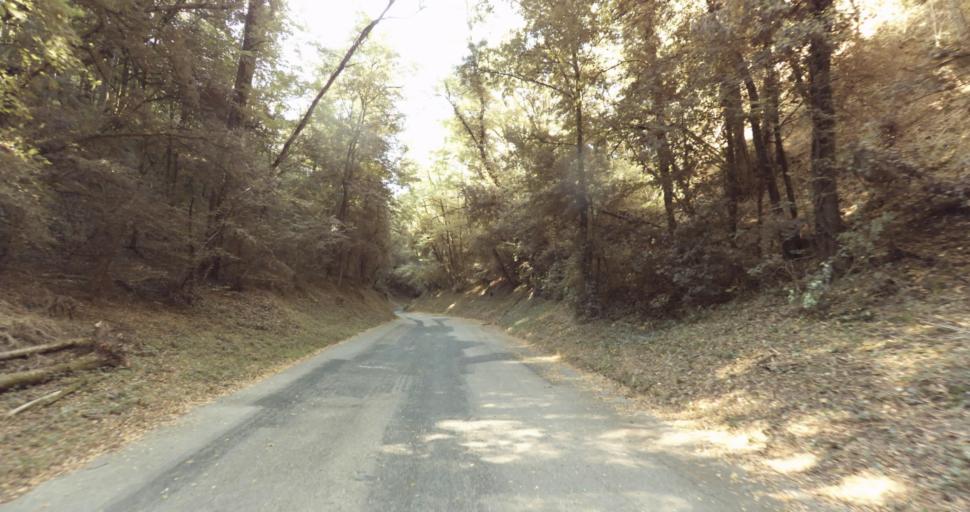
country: FR
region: Rhone-Alpes
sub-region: Departement du Rhone
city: Genay
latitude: 45.8869
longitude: 4.8410
